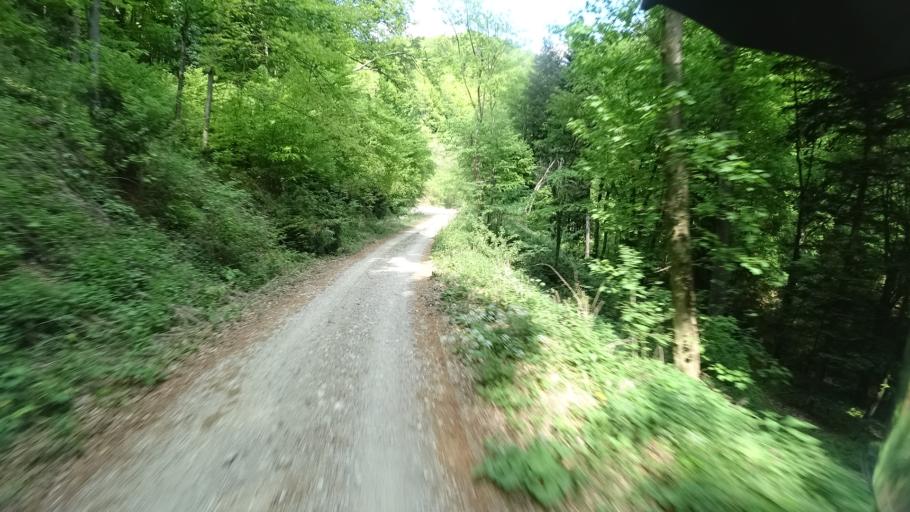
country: HR
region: Grad Zagreb
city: Kasina
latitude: 45.9240
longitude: 16.0223
